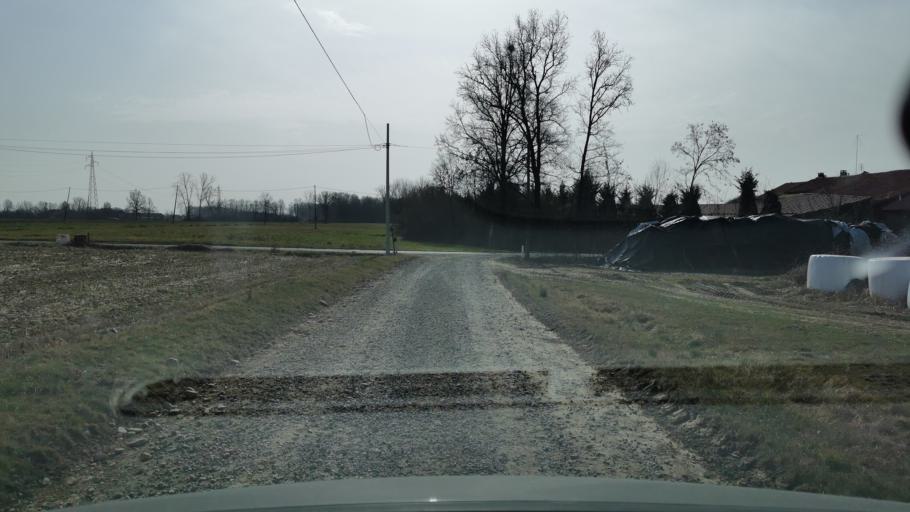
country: IT
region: Piedmont
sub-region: Provincia di Torino
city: Rivarossa
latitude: 45.2637
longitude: 7.7188
